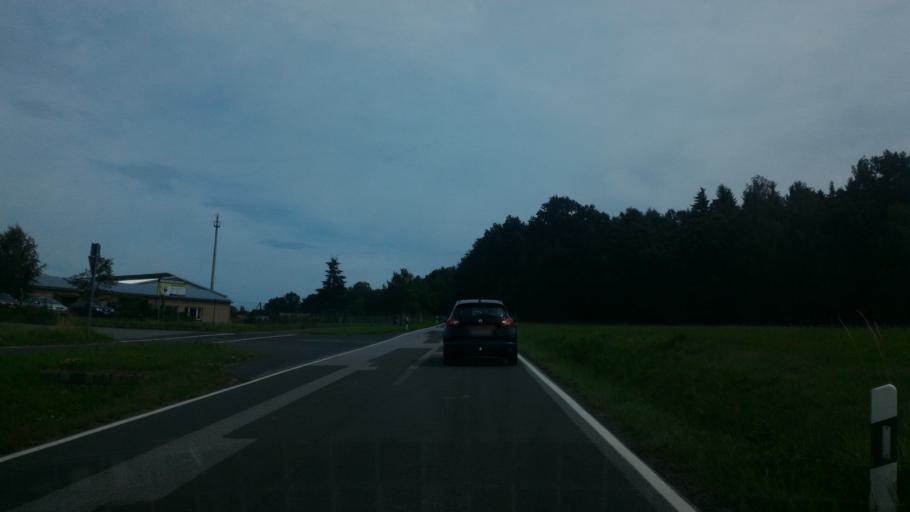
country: DE
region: Saxony
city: Bertsdorf-Hoernitz
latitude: 50.8727
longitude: 14.7397
